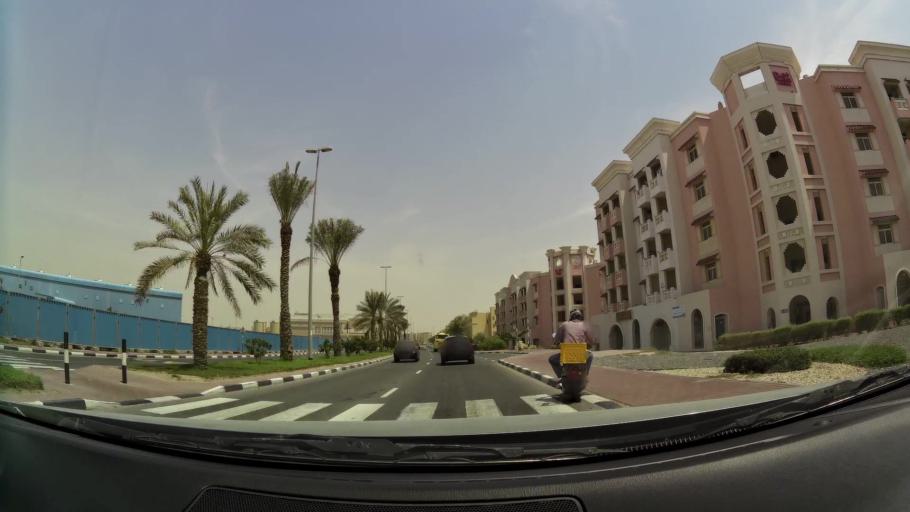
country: AE
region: Ash Shariqah
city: Sharjah
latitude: 25.1671
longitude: 55.4167
